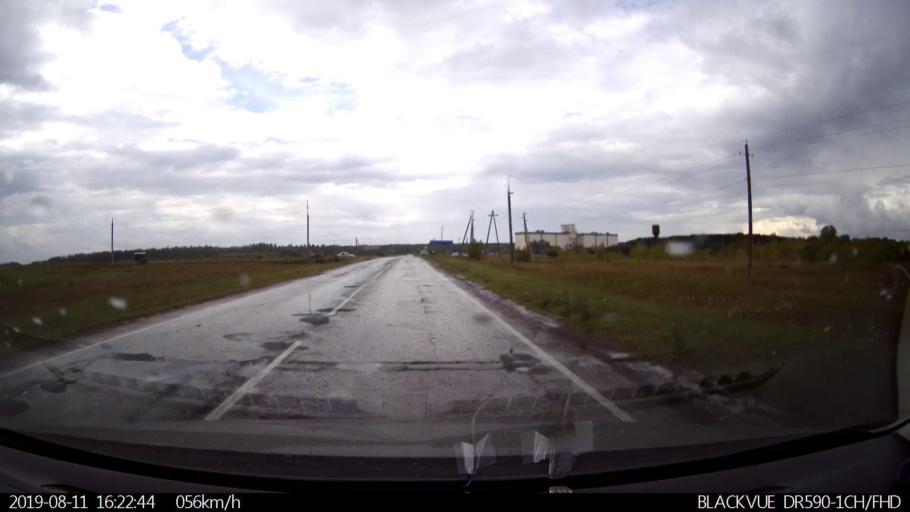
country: RU
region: Ulyanovsk
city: Mayna
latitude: 54.0905
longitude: 47.5914
